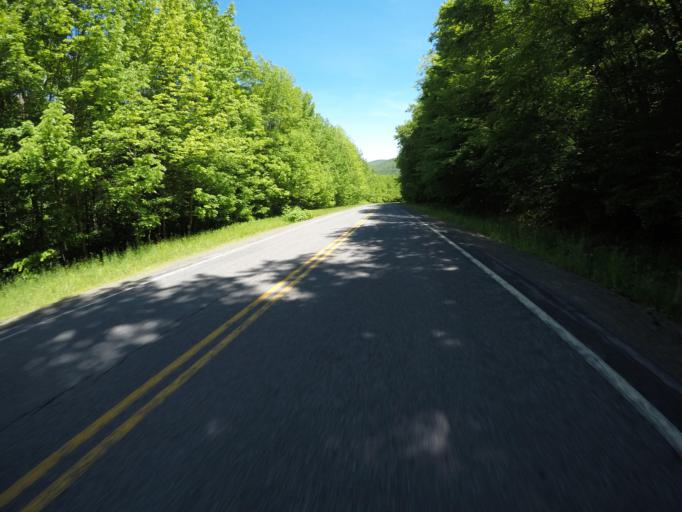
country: US
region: New York
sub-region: Delaware County
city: Delhi
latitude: 42.1984
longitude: -74.8254
